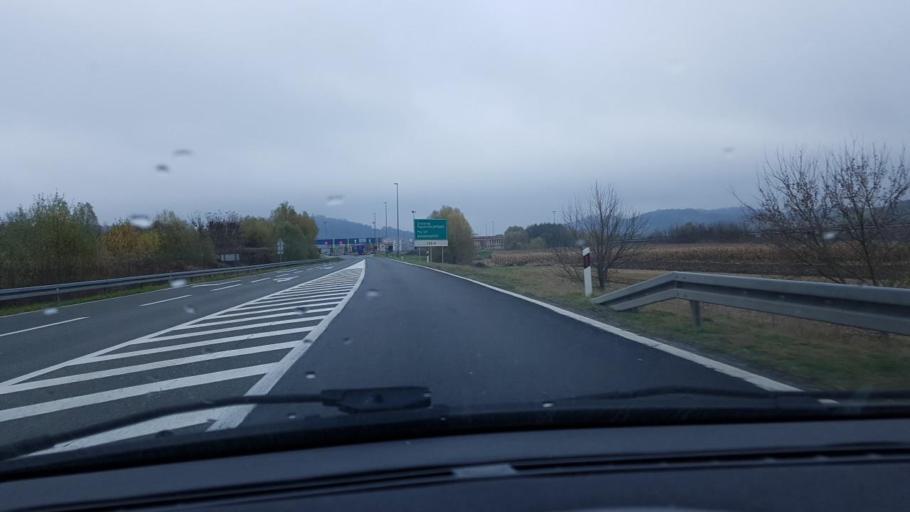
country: HR
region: Krapinsko-Zagorska
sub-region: Grad Krapina
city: Krapina
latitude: 46.1358
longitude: 15.8811
